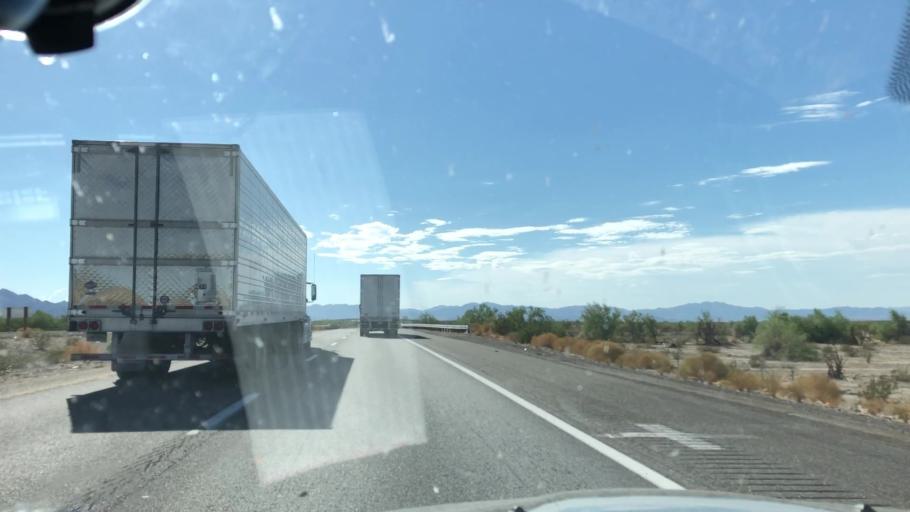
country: US
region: California
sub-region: Riverside County
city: Mesa Verde
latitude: 33.6772
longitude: -115.2253
